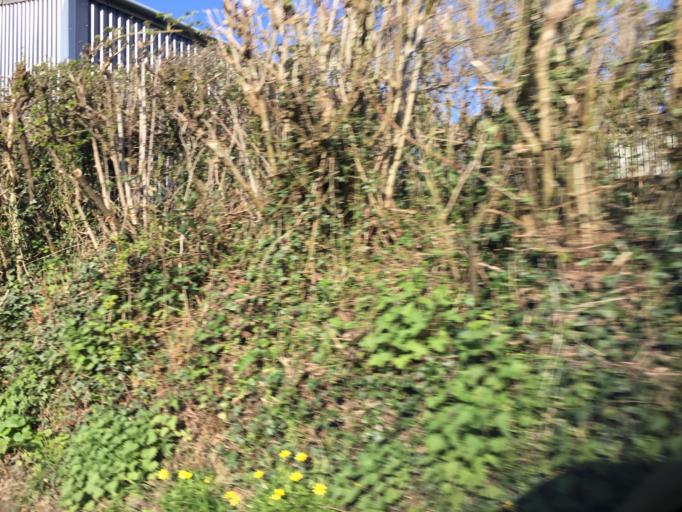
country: GB
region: Wales
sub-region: Torfaen County Borough
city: New Inn
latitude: 51.7011
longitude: -2.9844
